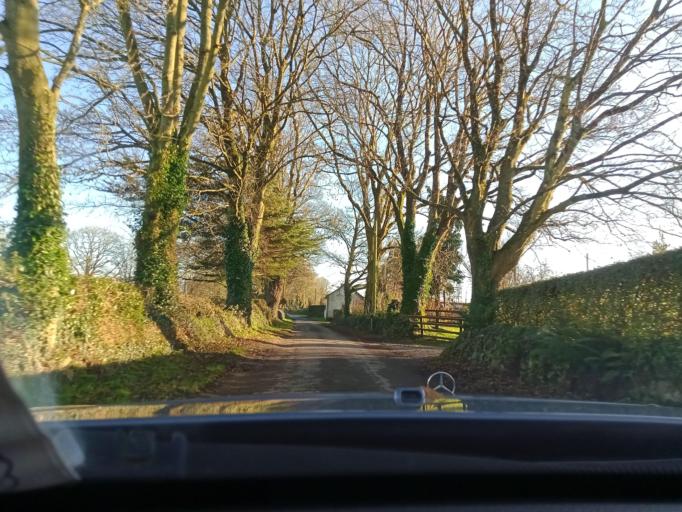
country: IE
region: Munster
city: Carrick-on-Suir
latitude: 52.4384
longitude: -7.3954
